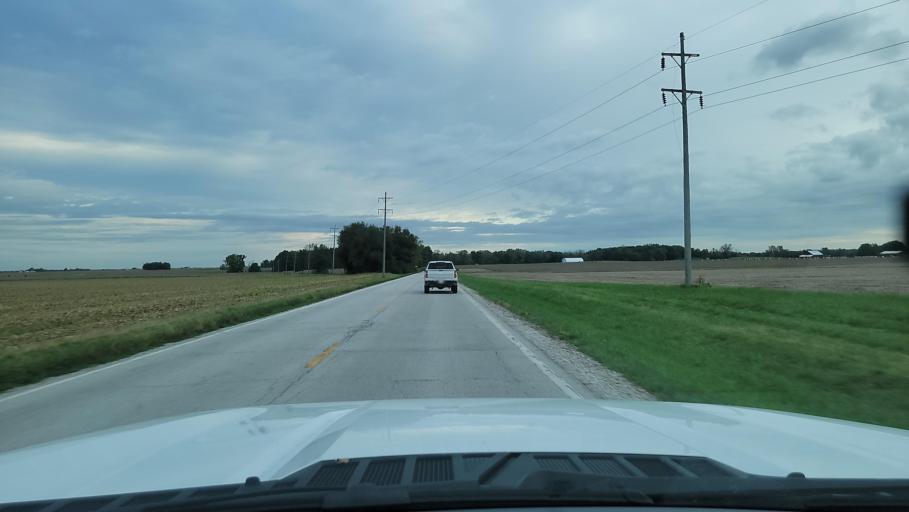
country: US
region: Illinois
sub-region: Schuyler County
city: Rushville
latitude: 40.1465
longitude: -90.5575
